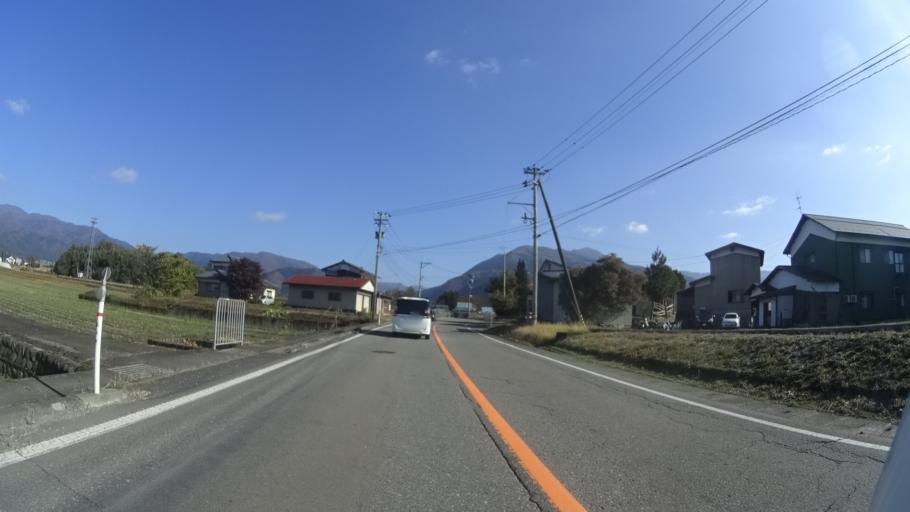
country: JP
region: Fukui
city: Ono
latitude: 35.9772
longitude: 136.5420
